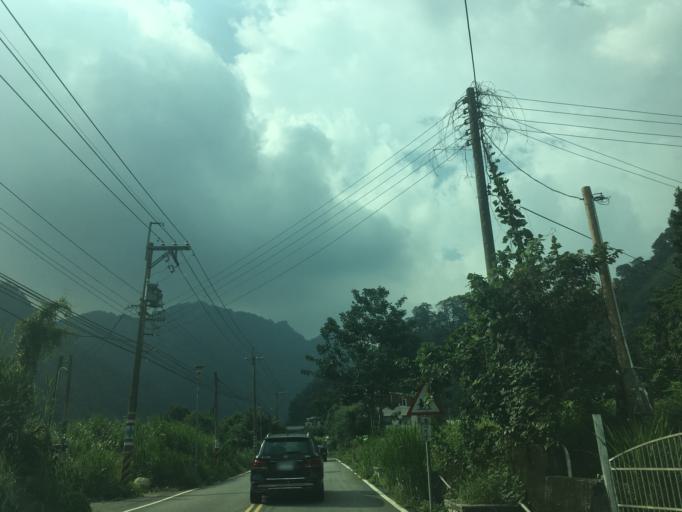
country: TW
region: Taiwan
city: Fengyuan
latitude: 24.3253
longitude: 120.9215
